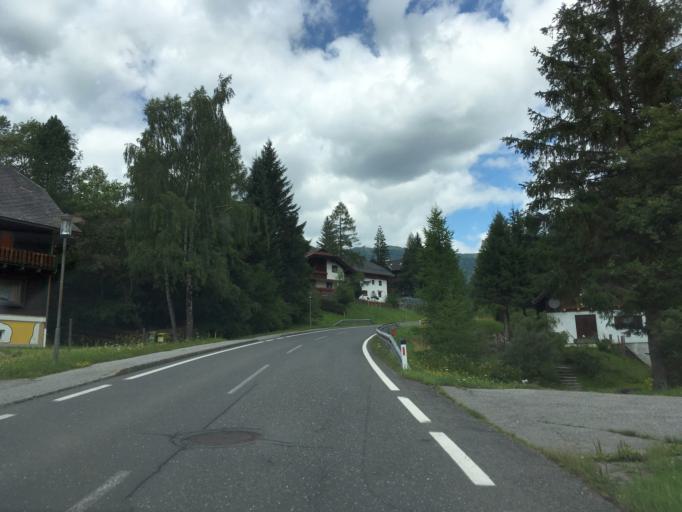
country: AT
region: Carinthia
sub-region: Politischer Bezirk Spittal an der Drau
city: Kleinkirchheim
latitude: 46.8274
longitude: 13.7698
